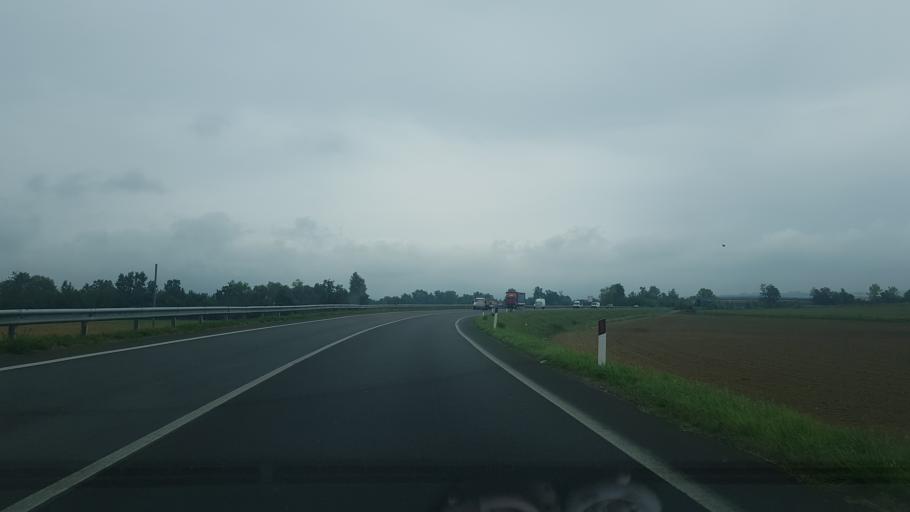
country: IT
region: Piedmont
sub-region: Provincia di Cuneo
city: Breo
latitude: 44.4176
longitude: 7.8076
